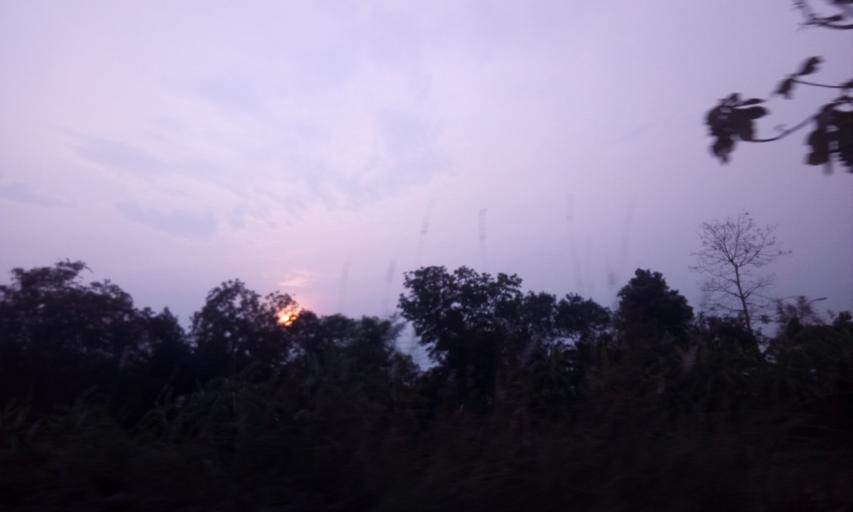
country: TH
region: Bangkok
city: Nong Chok
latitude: 13.9393
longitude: 100.8945
